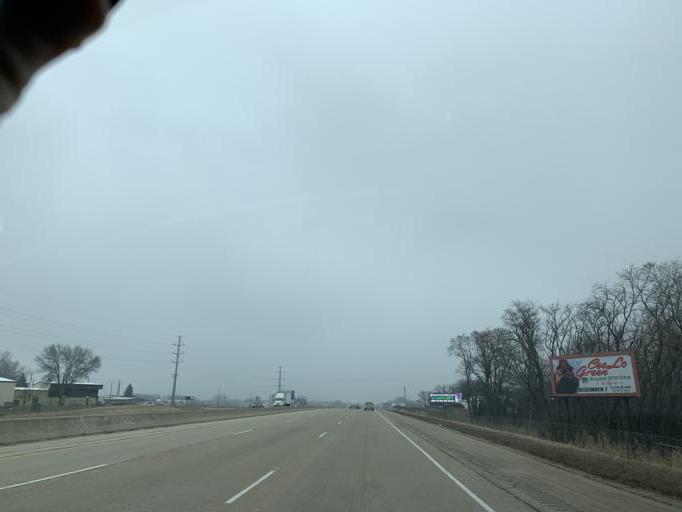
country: US
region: Wisconsin
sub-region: Dane County
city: Sun Prairie
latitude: 43.1669
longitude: -89.2607
